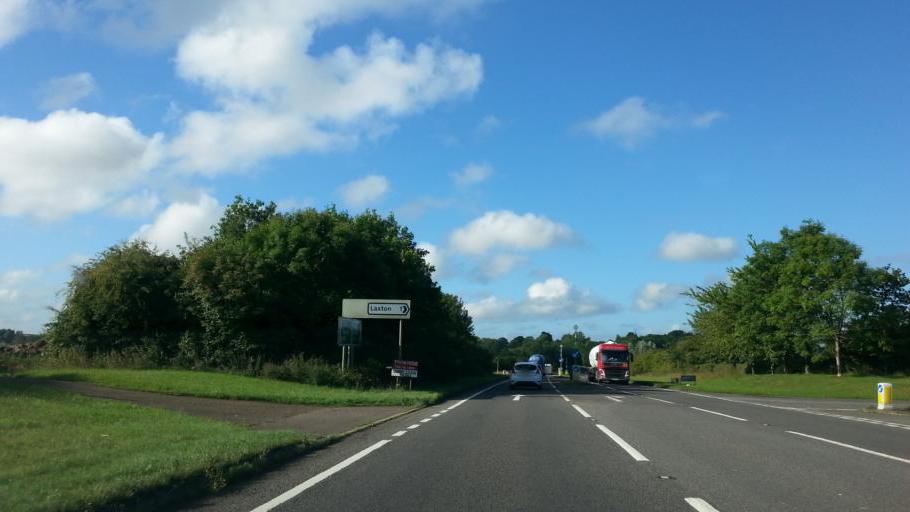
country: GB
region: England
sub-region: District of Rutland
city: South Luffenham
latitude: 52.5444
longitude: -0.5853
